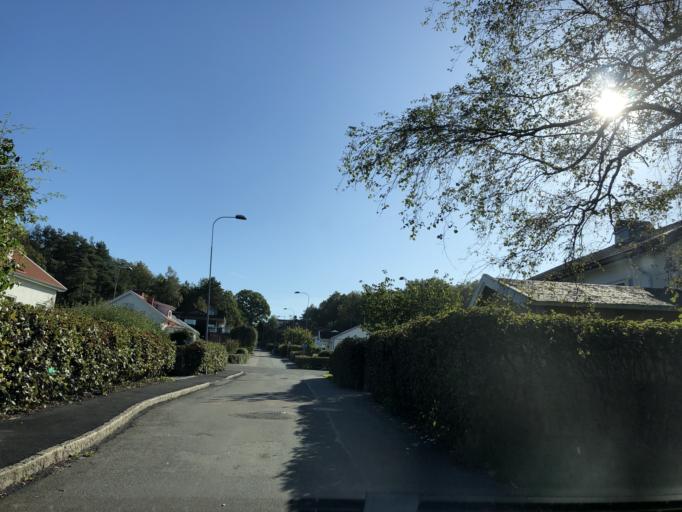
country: SE
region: Vaestra Goetaland
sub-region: Goteborg
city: Majorna
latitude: 57.6603
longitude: 11.8632
